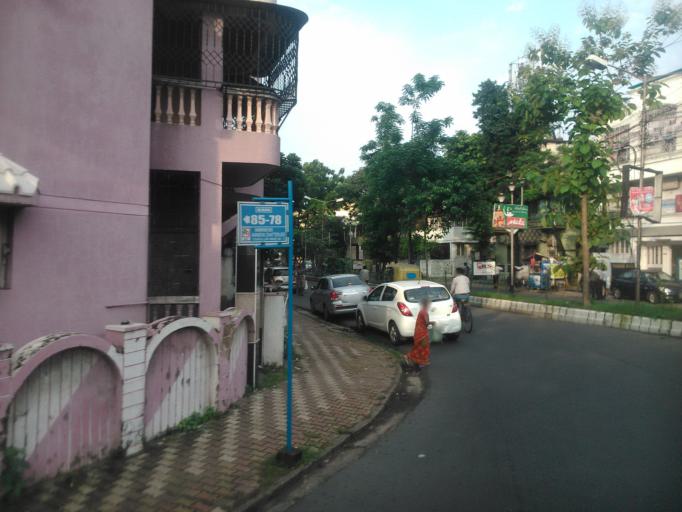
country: IN
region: West Bengal
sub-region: North 24 Parganas
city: Garui
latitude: 22.5949
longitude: 88.4051
